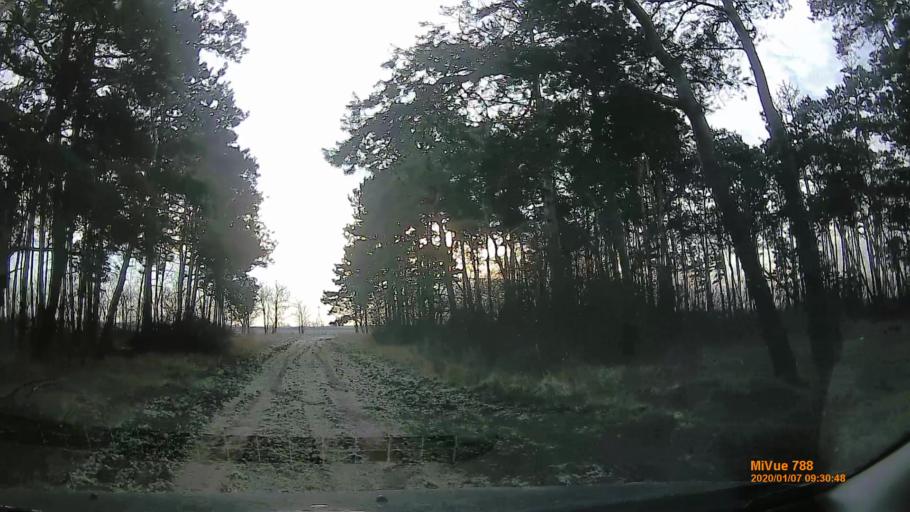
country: HU
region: Gyor-Moson-Sopron
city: Rajka
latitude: 47.9470
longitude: 17.1730
